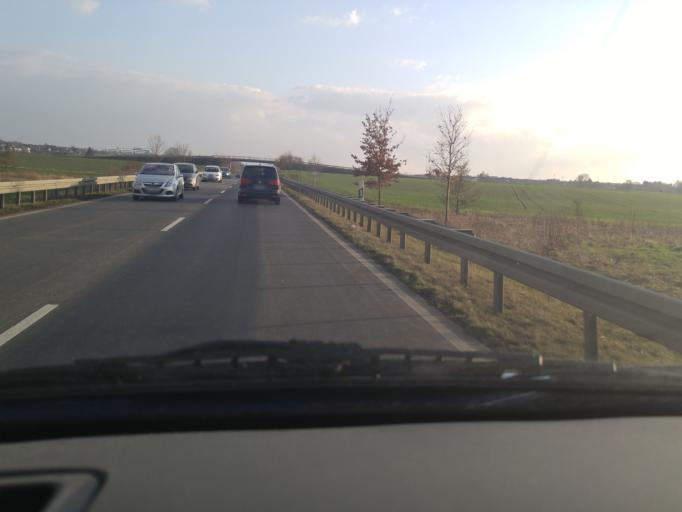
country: DE
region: Hesse
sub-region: Regierungsbezirk Darmstadt
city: Friedberg
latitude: 50.3408
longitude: 8.7349
